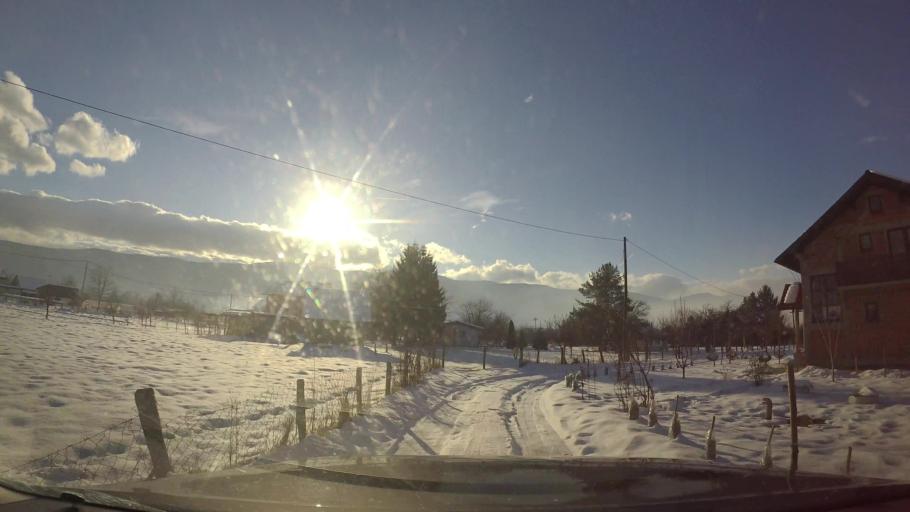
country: BA
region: Federation of Bosnia and Herzegovina
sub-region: Kanton Sarajevo
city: Sarajevo
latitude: 43.8110
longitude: 18.3458
